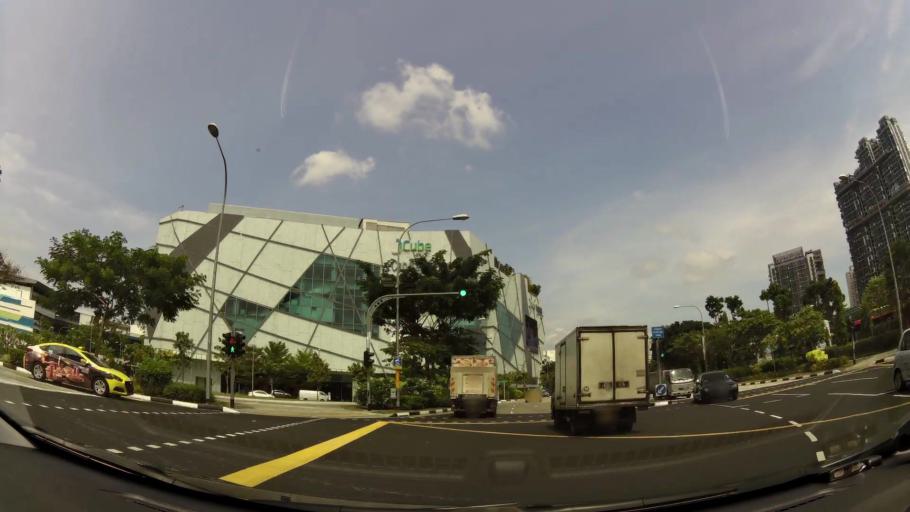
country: SG
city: Singapore
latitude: 1.3326
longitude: 103.7410
